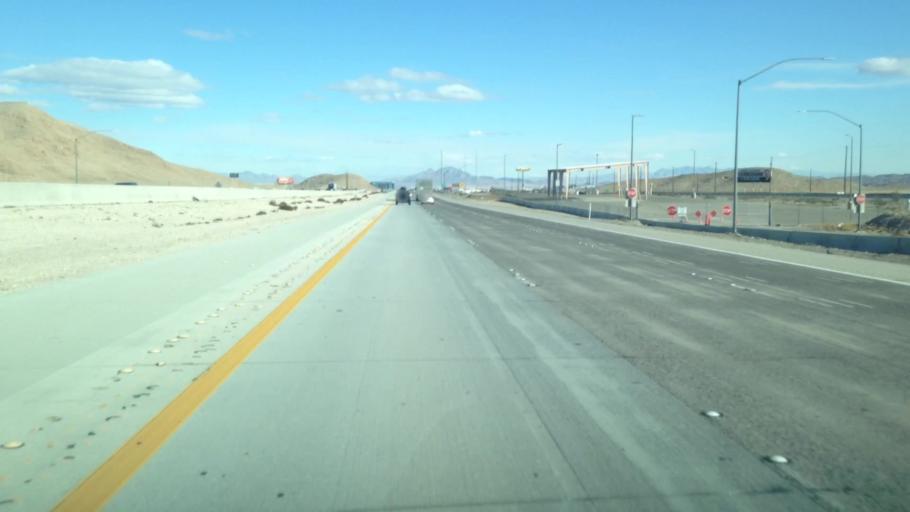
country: US
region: Nevada
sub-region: Clark County
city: Enterprise
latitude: 35.9259
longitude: -115.1960
